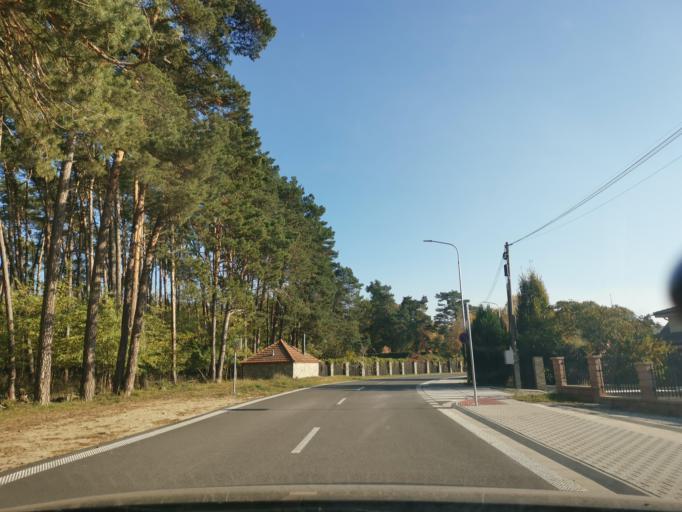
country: SK
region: Bratislavsky
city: Stupava
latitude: 48.3303
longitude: 17.0583
